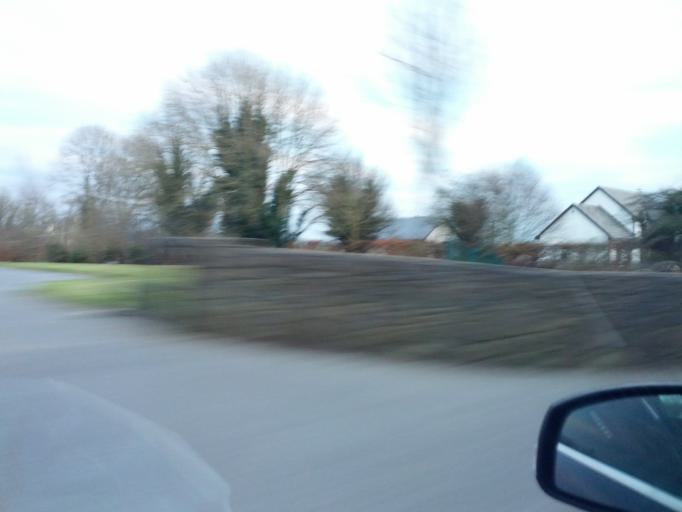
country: IE
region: Connaught
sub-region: County Galway
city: Athenry
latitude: 53.3288
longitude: -8.7666
